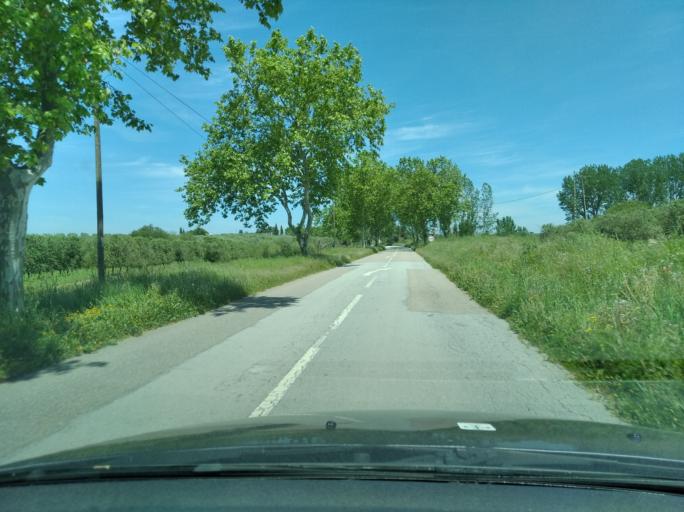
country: PT
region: Portalegre
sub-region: Avis
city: Avis
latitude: 39.0833
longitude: -7.8795
